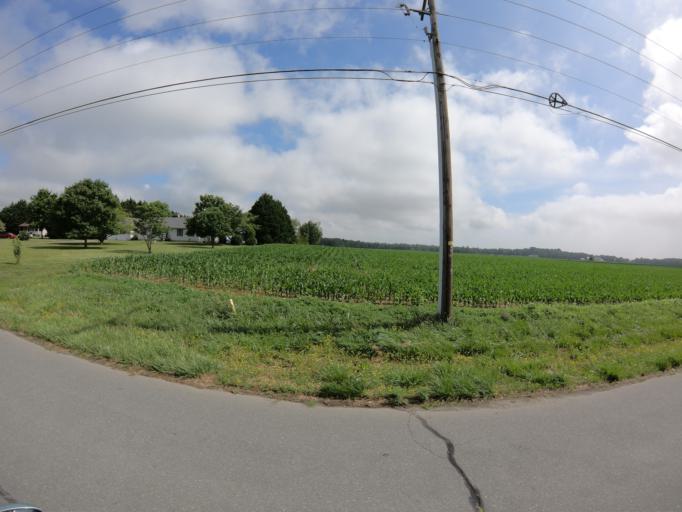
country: US
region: Delaware
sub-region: Kent County
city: Riverview
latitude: 39.0098
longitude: -75.4831
